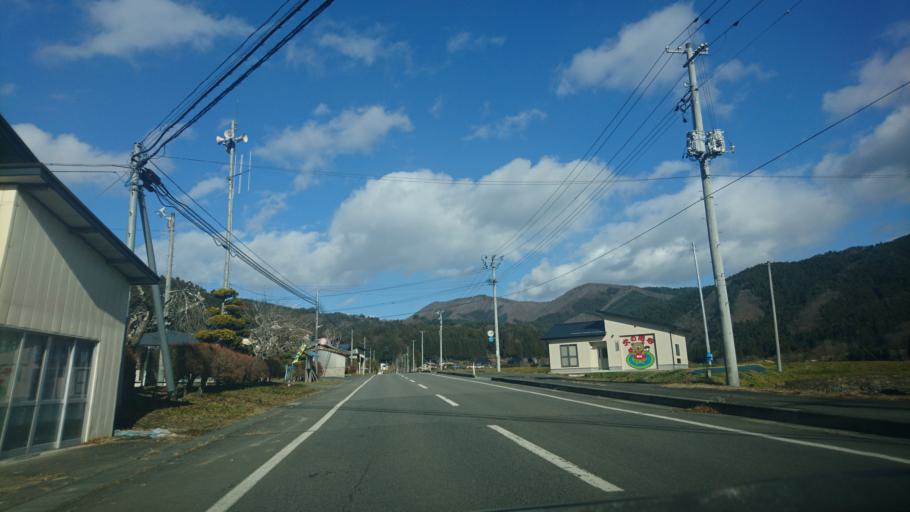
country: JP
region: Iwate
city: Mizusawa
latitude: 39.0700
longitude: 141.3809
